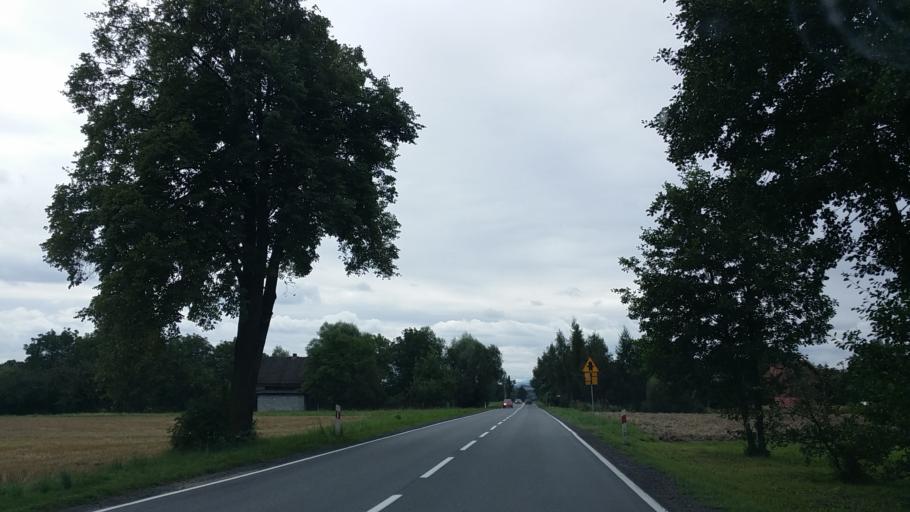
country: PL
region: Lesser Poland Voivodeship
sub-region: Powiat oswiecimski
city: Zator
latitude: 49.9787
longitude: 19.4390
